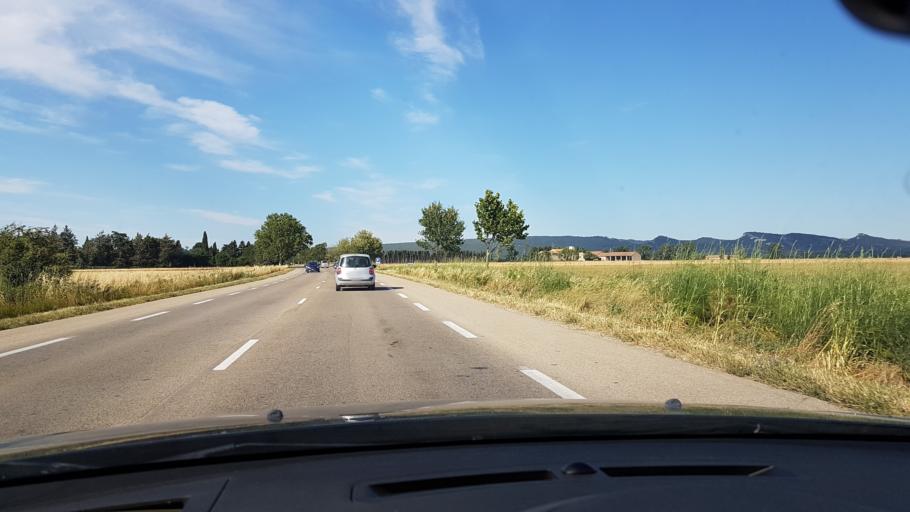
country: FR
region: Provence-Alpes-Cote d'Azur
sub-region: Departement des Bouches-du-Rhone
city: Fontvieille
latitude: 43.7316
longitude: 4.6646
